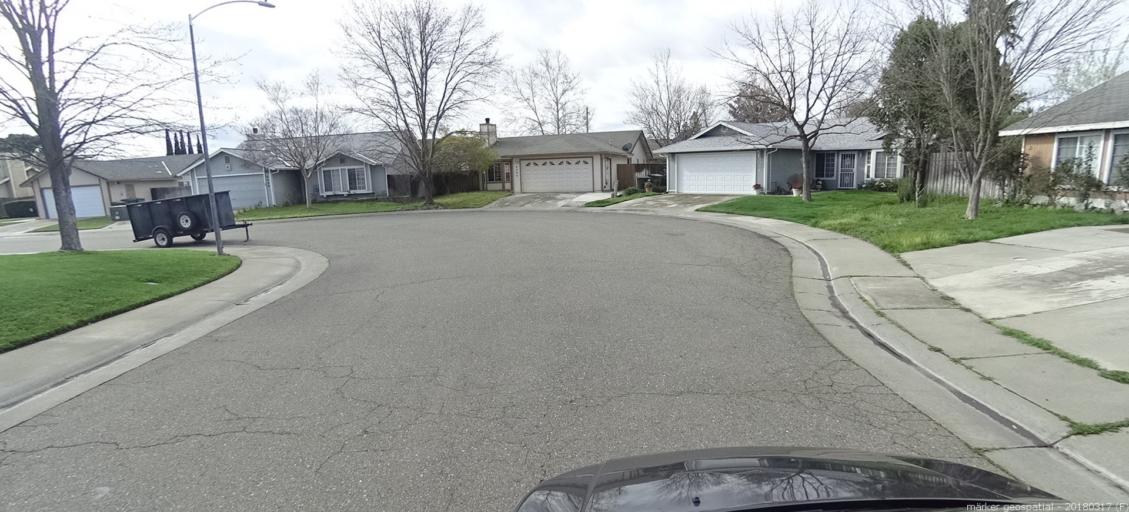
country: US
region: California
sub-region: Sacramento County
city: Florin
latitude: 38.4663
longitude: -121.3945
